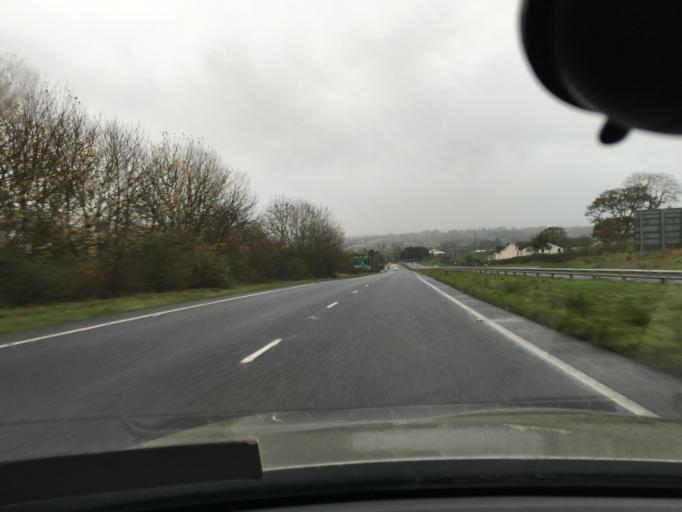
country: GB
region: Northern Ireland
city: Carnmoney
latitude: 54.7095
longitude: -5.9677
